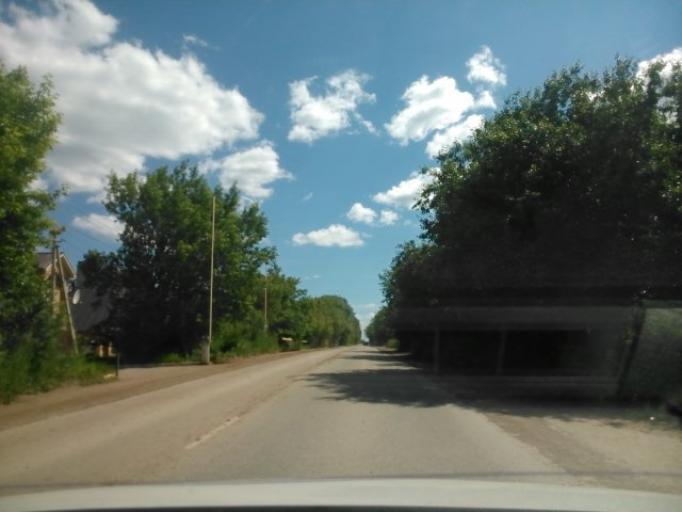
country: RU
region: Perm
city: Perm
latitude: 58.0034
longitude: 56.3292
